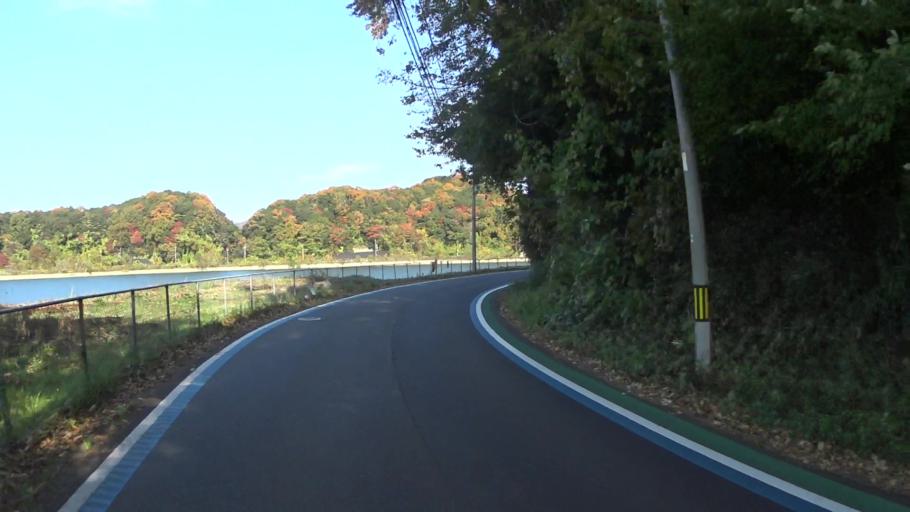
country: JP
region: Kyoto
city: Maizuru
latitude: 35.4797
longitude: 135.3460
